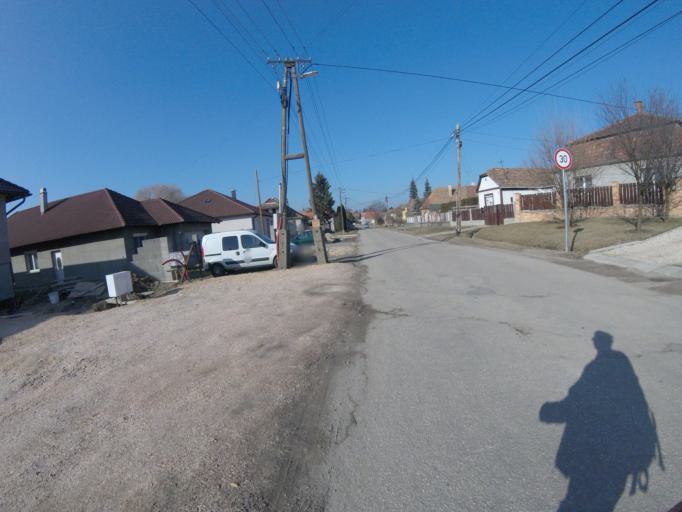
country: HU
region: Komarom-Esztergom
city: Oroszlany
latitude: 47.4829
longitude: 18.3281
